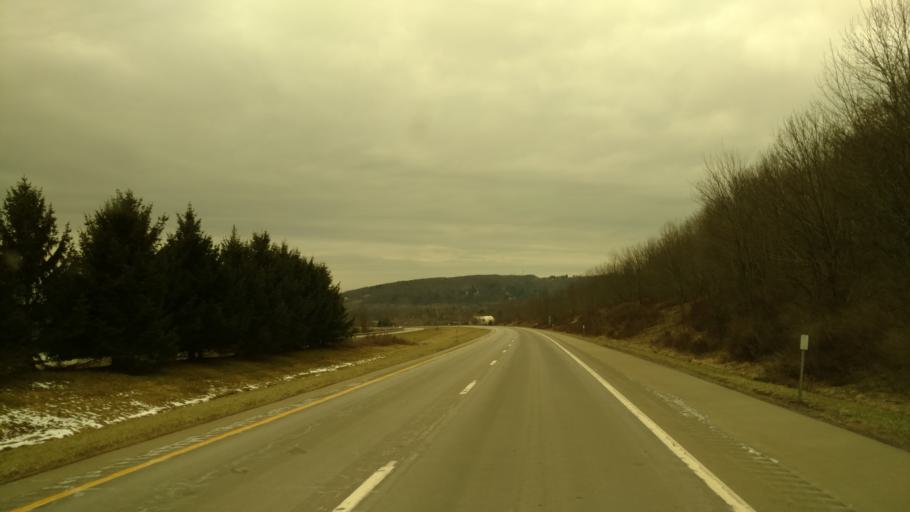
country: US
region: New York
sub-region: Chautauqua County
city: Falconer
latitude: 42.1381
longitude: -79.1720
